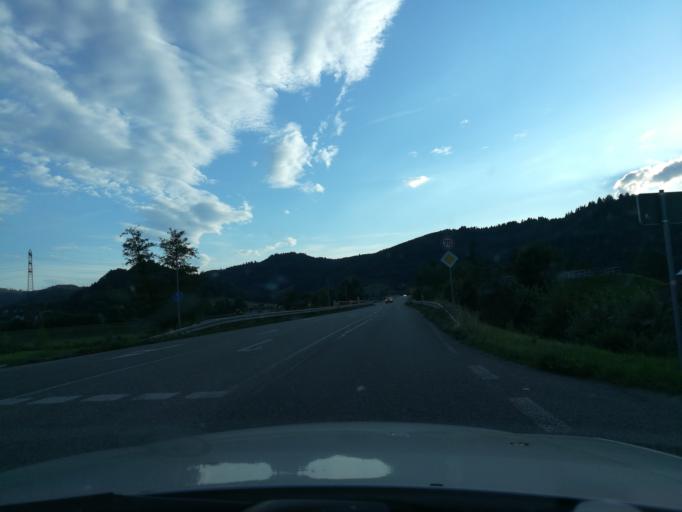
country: DE
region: Baden-Wuerttemberg
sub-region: Freiburg Region
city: Berghaupten
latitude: 48.4155
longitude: 7.9944
